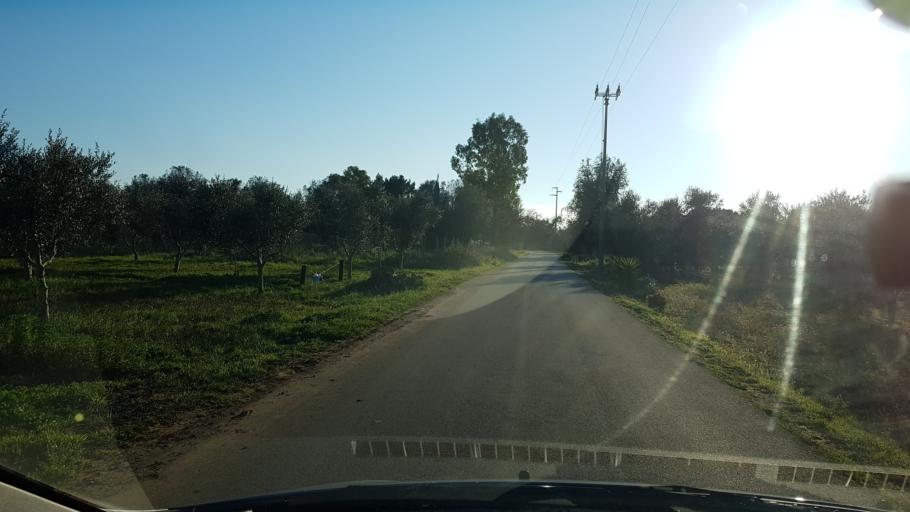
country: IT
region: Apulia
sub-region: Provincia di Brindisi
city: Mesagne
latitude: 40.5780
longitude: 17.8771
